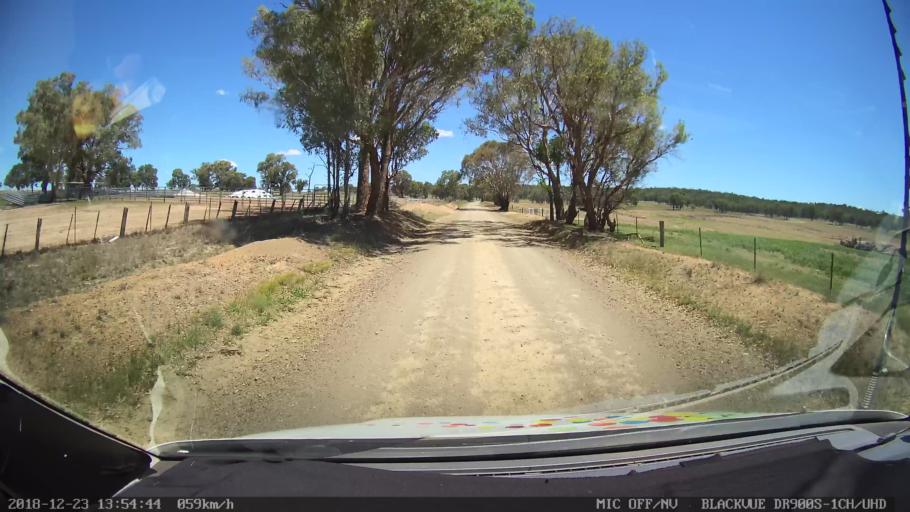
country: AU
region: New South Wales
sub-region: Tamworth Municipality
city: Manilla
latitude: -30.5638
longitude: 151.0901
